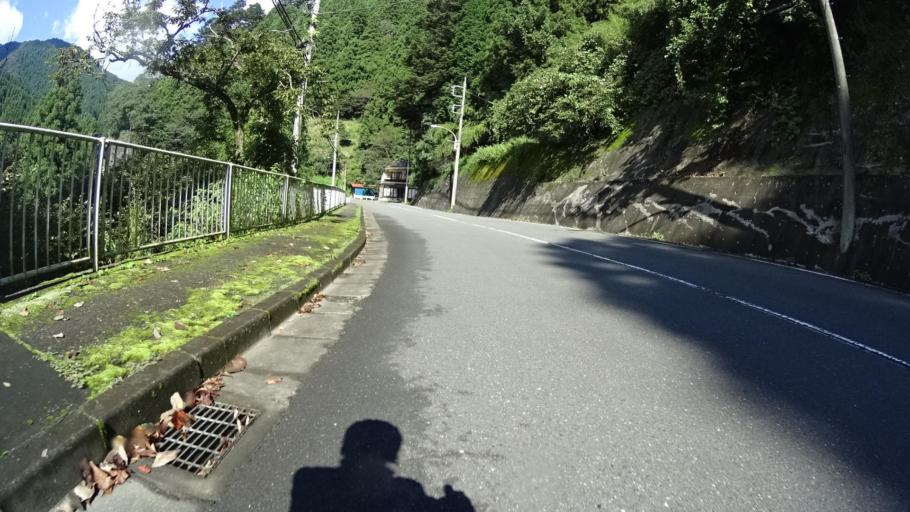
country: JP
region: Yamanashi
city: Uenohara
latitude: 35.7351
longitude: 139.0973
